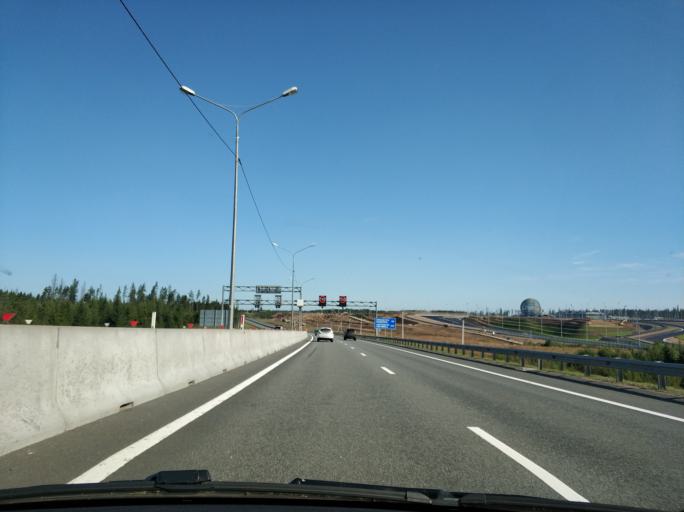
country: RU
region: Leningrad
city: Sosnovo
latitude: 60.5037
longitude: 30.1942
